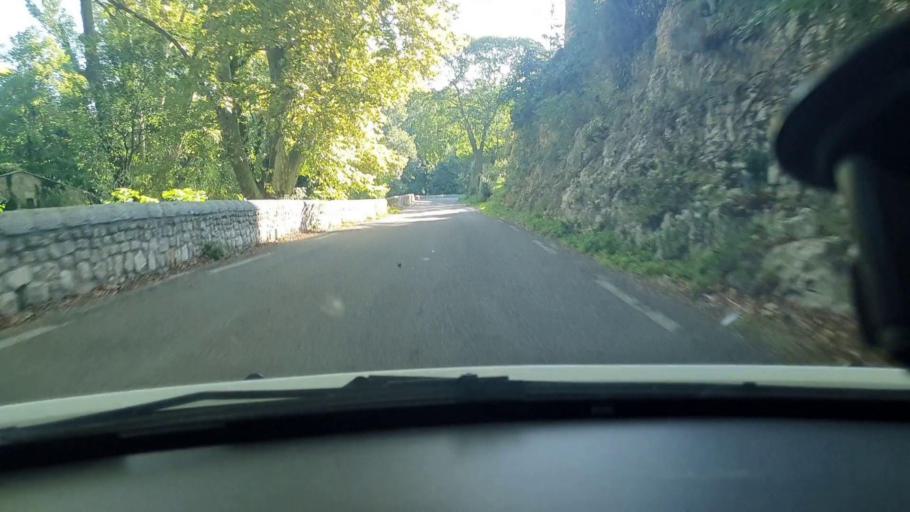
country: FR
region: Languedoc-Roussillon
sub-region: Departement du Gard
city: Goudargues
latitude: 44.2038
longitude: 4.4672
